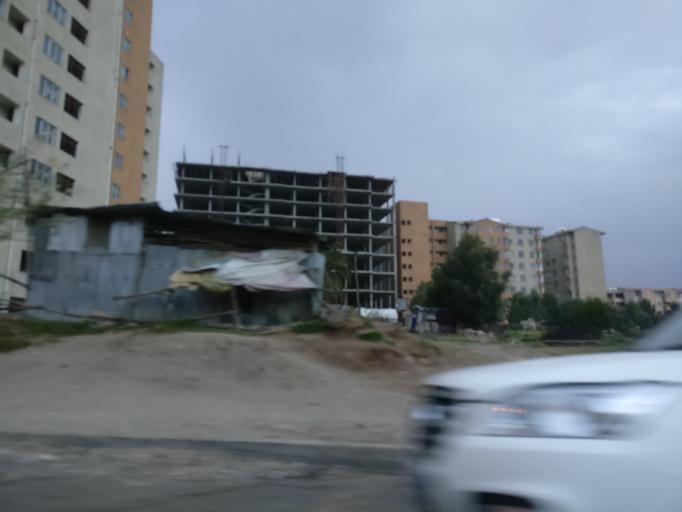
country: ET
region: Adis Abeba
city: Addis Ababa
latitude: 9.0165
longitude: 38.7355
